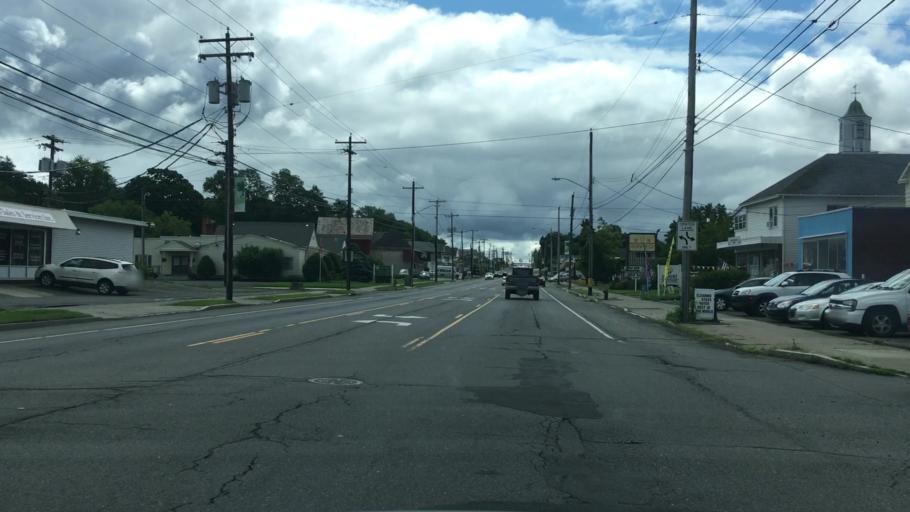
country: US
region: New York
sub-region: Schenectady County
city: Schenectady
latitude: 42.7791
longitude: -73.9026
